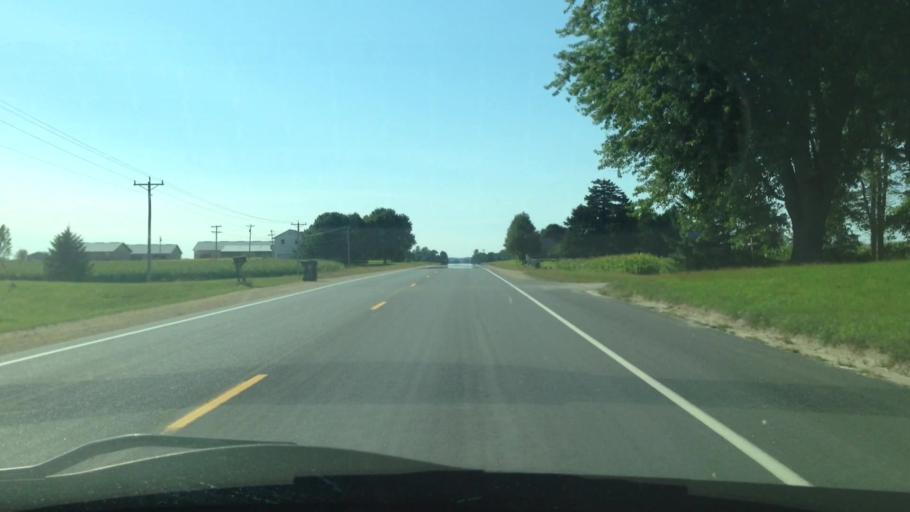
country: US
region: Minnesota
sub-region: Winona County
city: Lewiston
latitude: 43.9697
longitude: -91.8351
